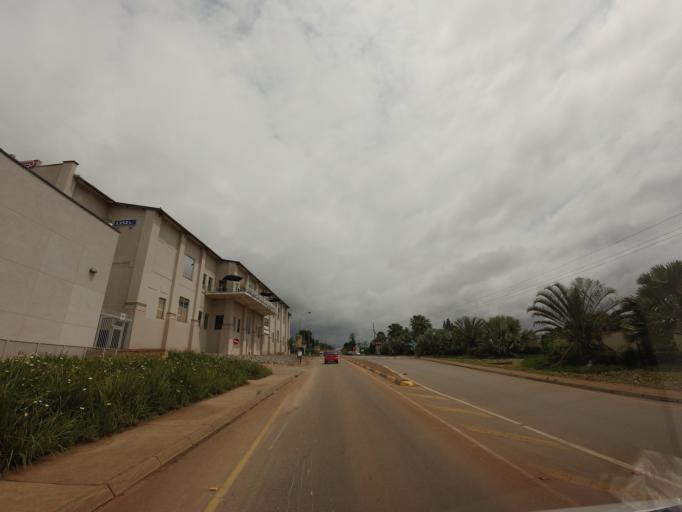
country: SZ
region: Hhohho
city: Lobamba
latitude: -26.4413
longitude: 31.1892
